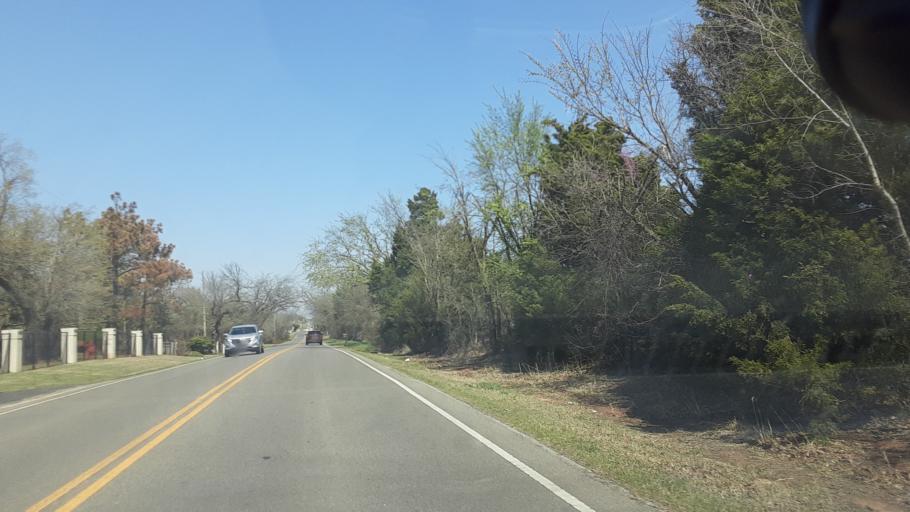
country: US
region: Oklahoma
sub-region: Oklahoma County
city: Edmond
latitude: 35.7202
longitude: -97.4783
